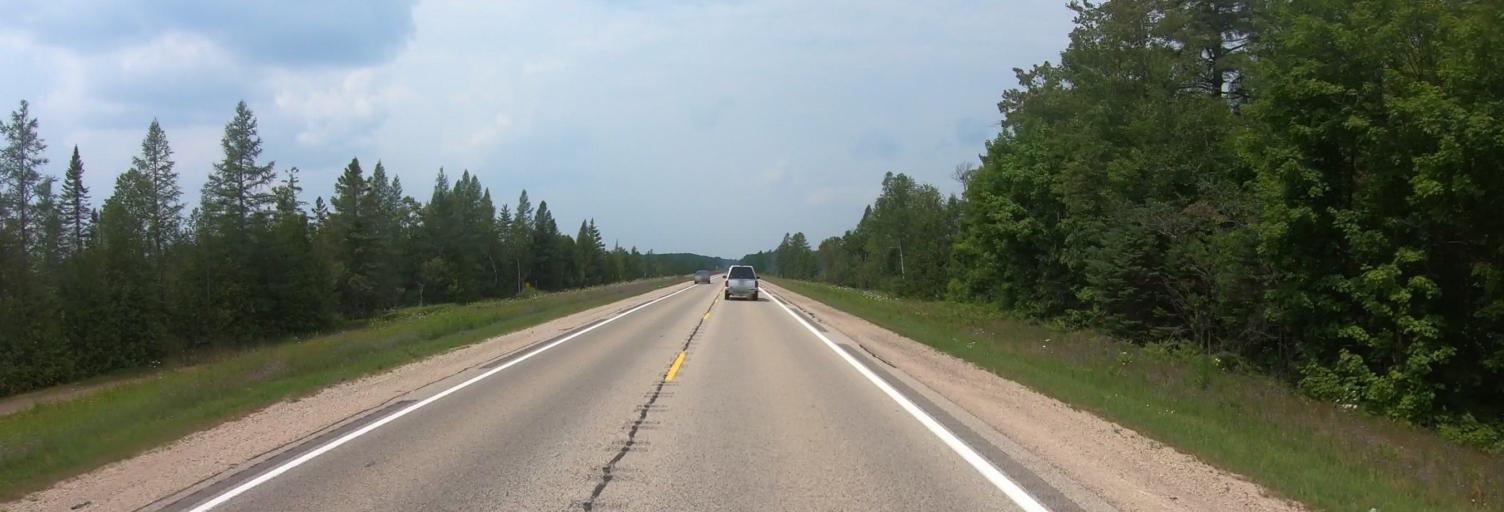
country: US
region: Michigan
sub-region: Alger County
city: Munising
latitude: 46.3762
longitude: -86.5631
